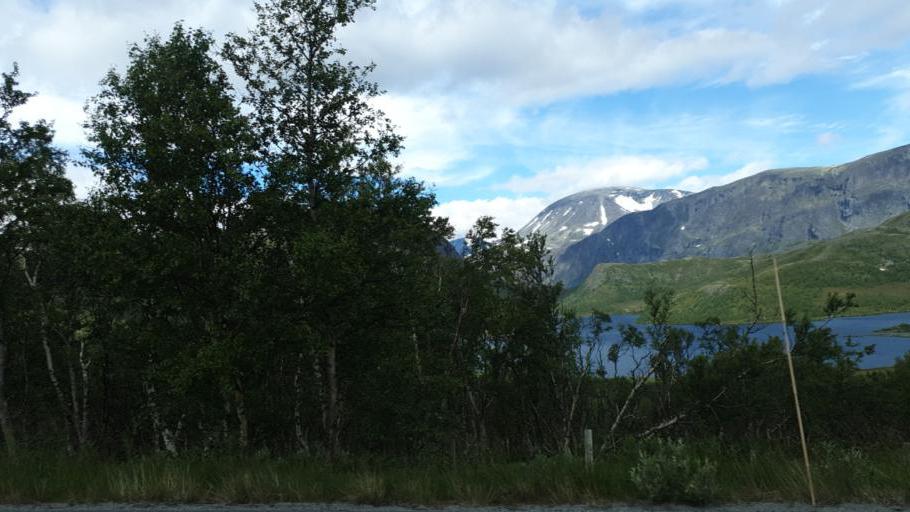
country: NO
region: Oppland
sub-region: Oystre Slidre
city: Heggenes
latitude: 61.4679
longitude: 8.8137
